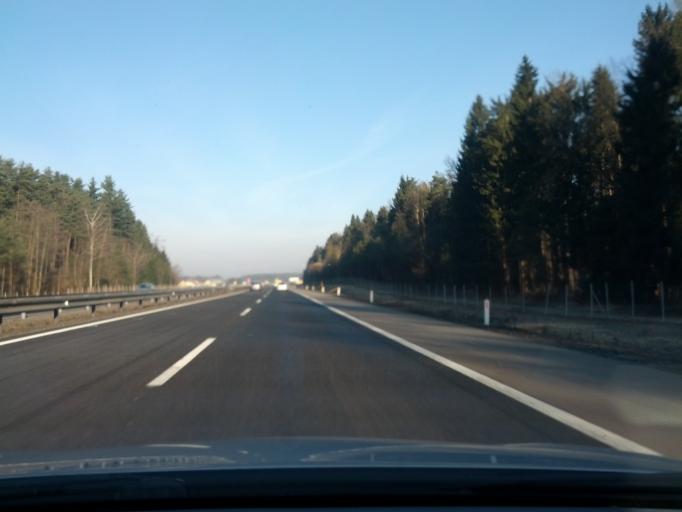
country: SI
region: Sencur
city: Sencur
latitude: 46.2111
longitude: 14.4517
